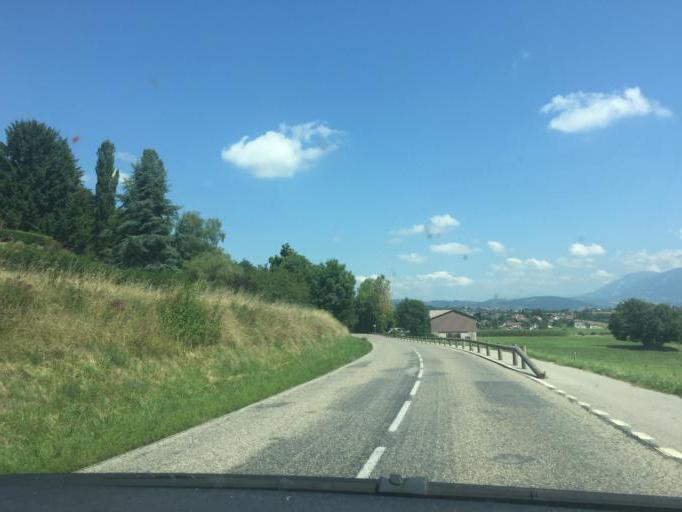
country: FR
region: Rhone-Alpes
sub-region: Departement de la Haute-Savoie
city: Lovagny
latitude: 45.9067
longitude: 6.0448
